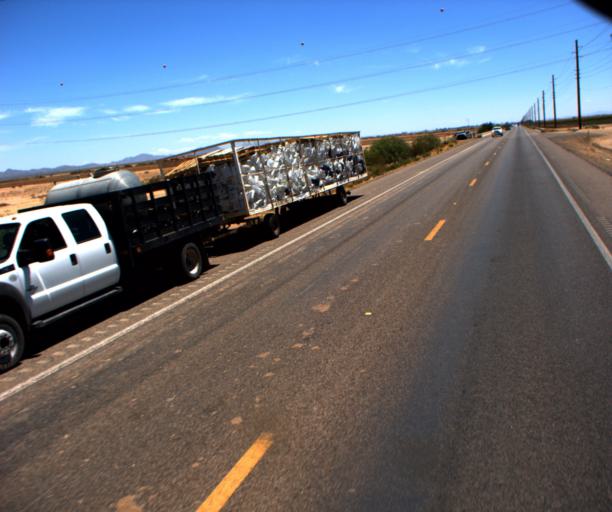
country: US
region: Arizona
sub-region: Pinal County
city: Casa Grande
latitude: 32.8794
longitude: -111.9482
